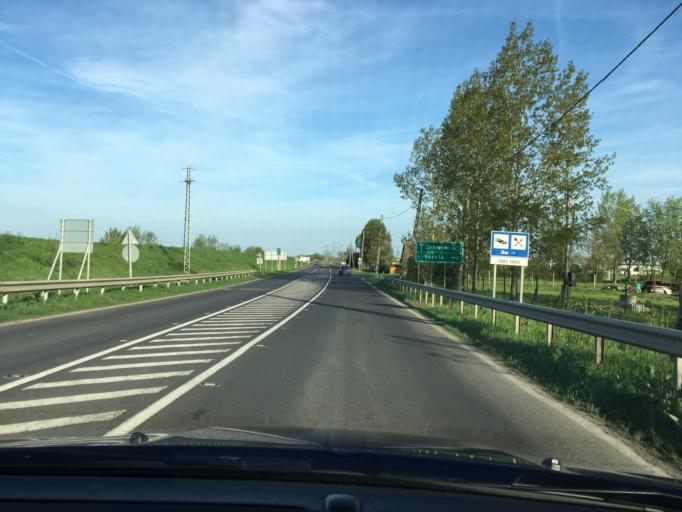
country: HU
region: Bekes
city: Szeghalom
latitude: 47.0125
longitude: 21.1809
